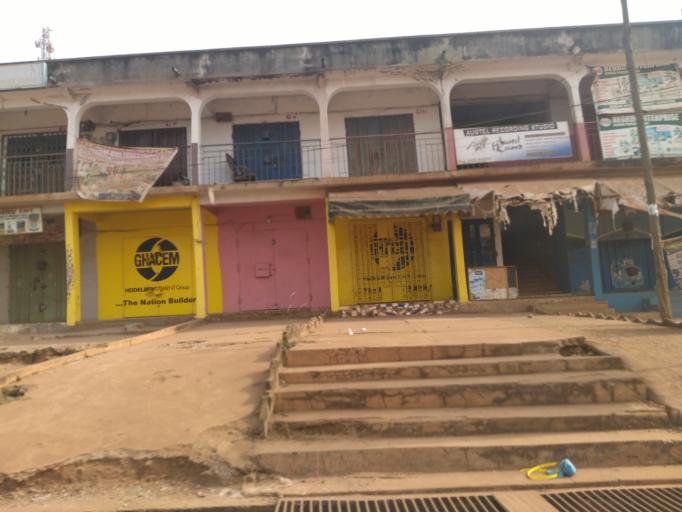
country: GH
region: Ashanti
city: Kumasi
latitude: 6.6486
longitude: -1.5826
